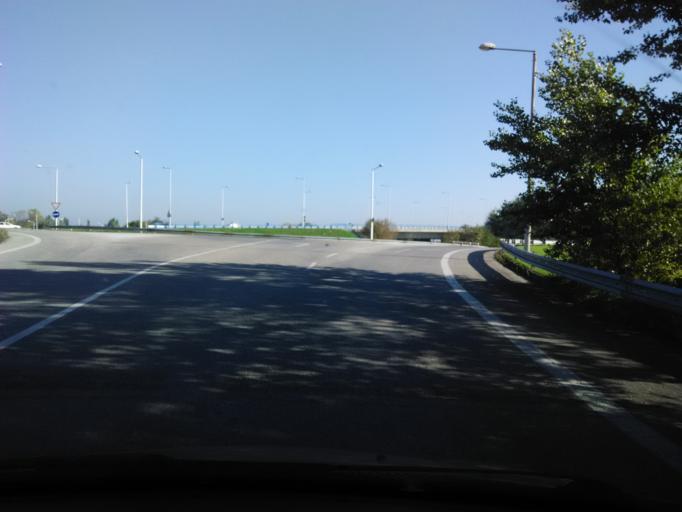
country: SK
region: Nitriansky
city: Komarno
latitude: 47.7638
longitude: 18.1073
